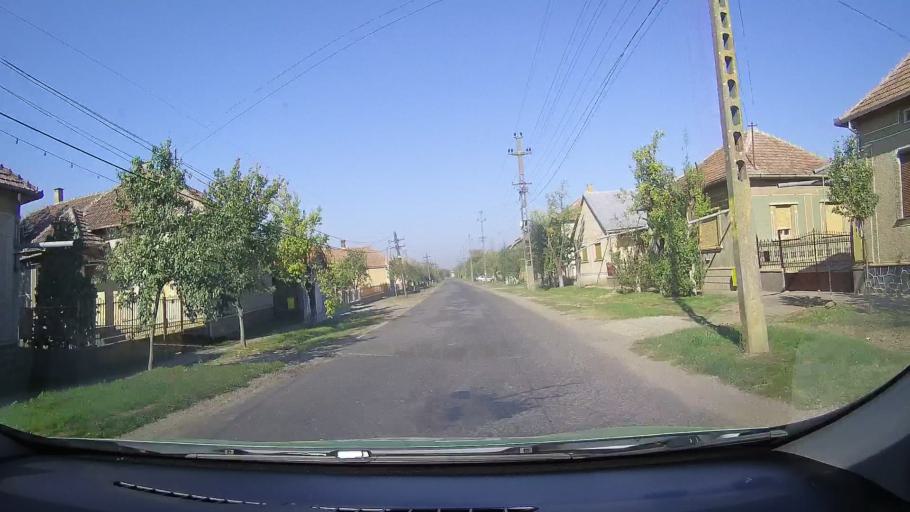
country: RO
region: Satu Mare
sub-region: Comuna Petresti
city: Petresti
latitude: 47.6064
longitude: 22.3607
